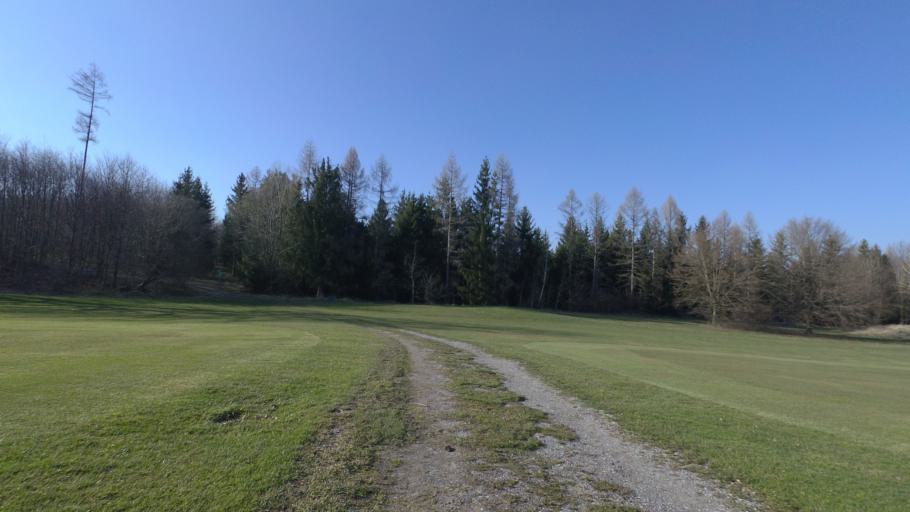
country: DE
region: Bavaria
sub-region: Upper Bavaria
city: Chieming
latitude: 47.9361
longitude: 12.5473
